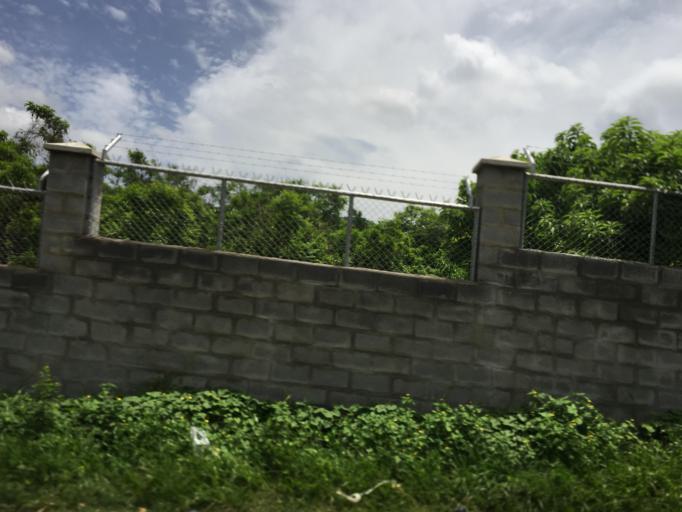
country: GT
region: Guatemala
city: Amatitlan
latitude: 14.4743
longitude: -90.5963
